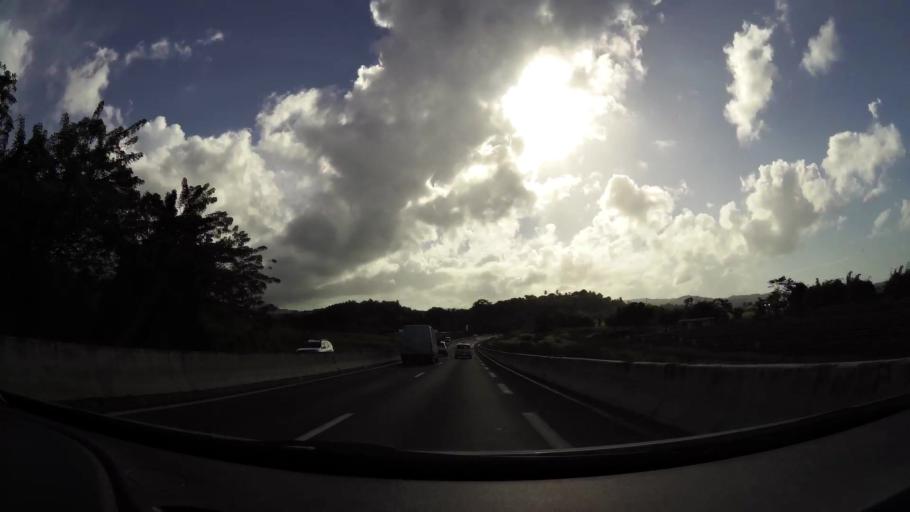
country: MQ
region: Martinique
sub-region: Martinique
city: Ducos
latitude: 14.5613
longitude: -60.9767
